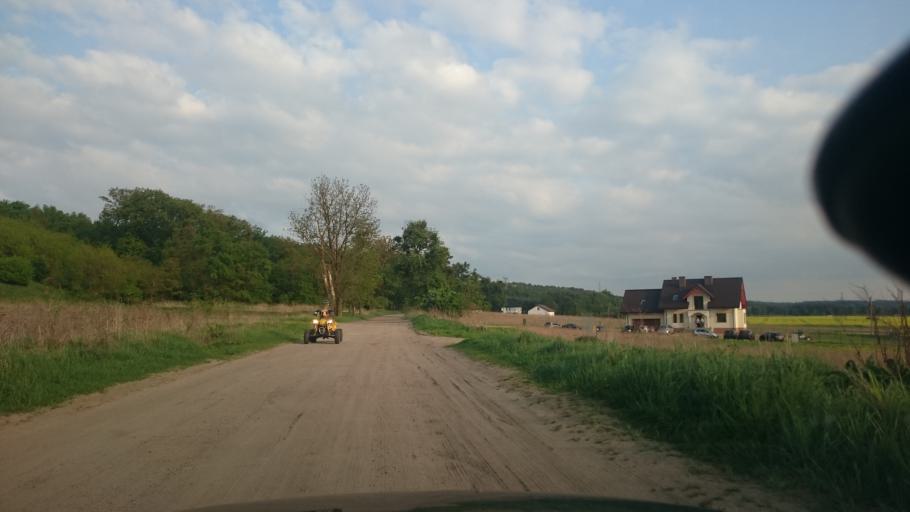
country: PL
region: Kujawsko-Pomorskie
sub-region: Grudziadz
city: Grudziadz
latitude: 53.4603
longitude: 18.8190
